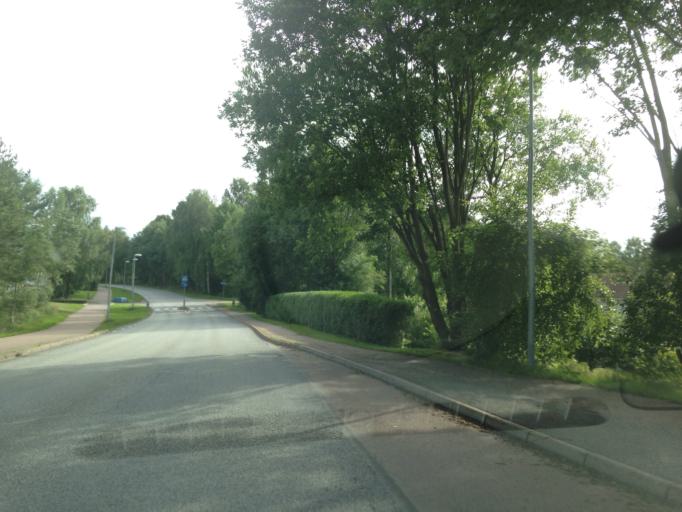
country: SE
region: Vaestra Goetaland
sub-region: Goteborg
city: Goeteborg
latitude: 57.7611
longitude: 11.9675
